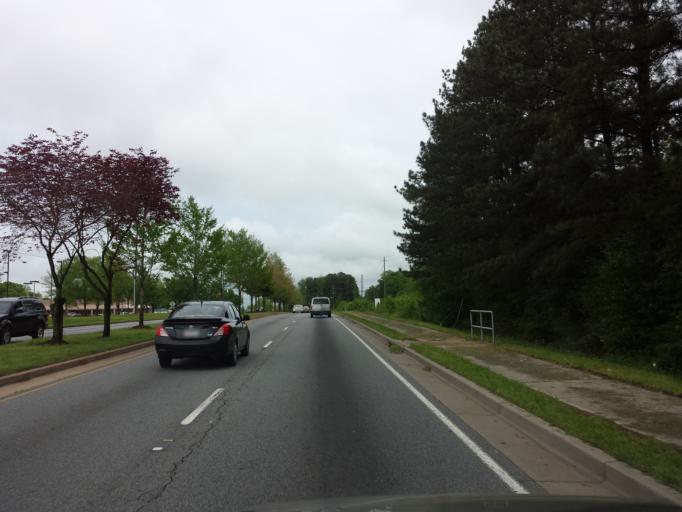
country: US
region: Georgia
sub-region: Cobb County
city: Mableton
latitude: 33.8552
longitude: -84.5965
